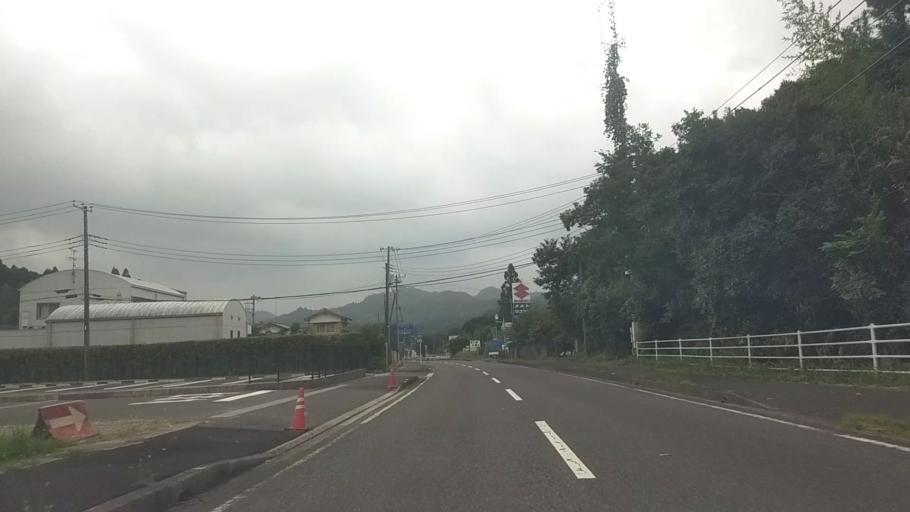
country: JP
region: Chiba
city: Kawaguchi
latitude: 35.2328
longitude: 140.0869
